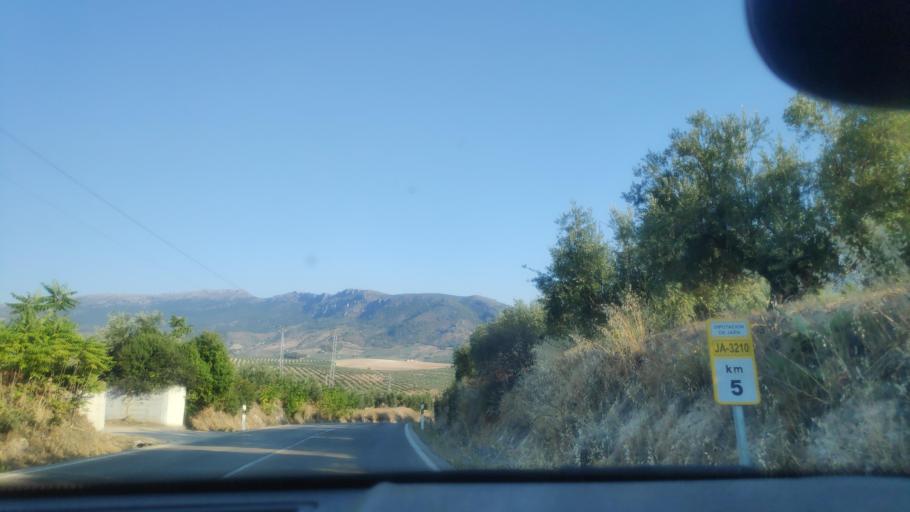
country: ES
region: Andalusia
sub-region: Provincia de Jaen
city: Jaen
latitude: 37.7293
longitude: -3.7630
